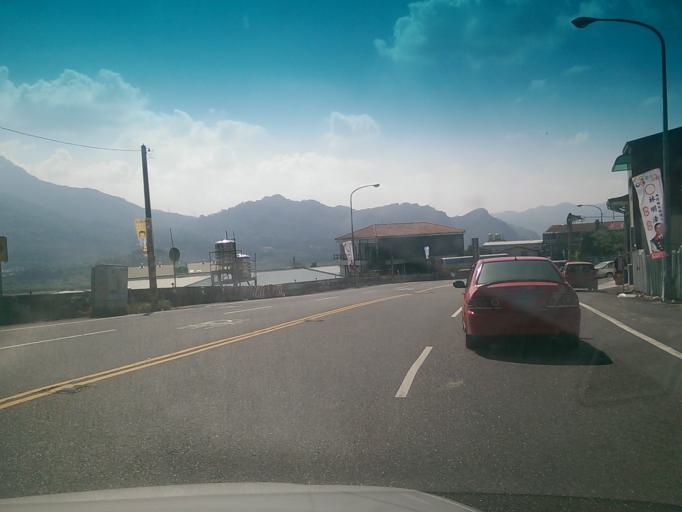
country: TW
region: Taiwan
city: Lugu
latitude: 23.8207
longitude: 120.8458
